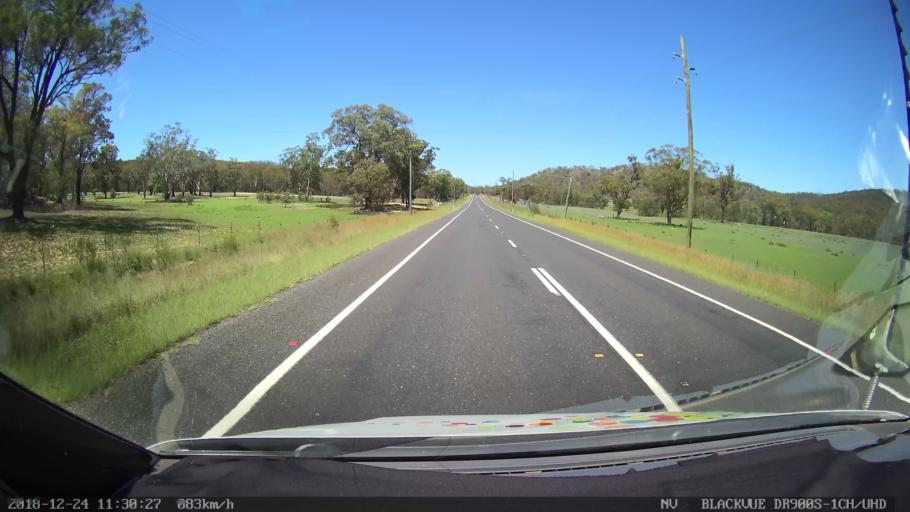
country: AU
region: New South Wales
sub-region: Upper Hunter Shire
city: Merriwa
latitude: -32.2049
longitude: 150.4662
